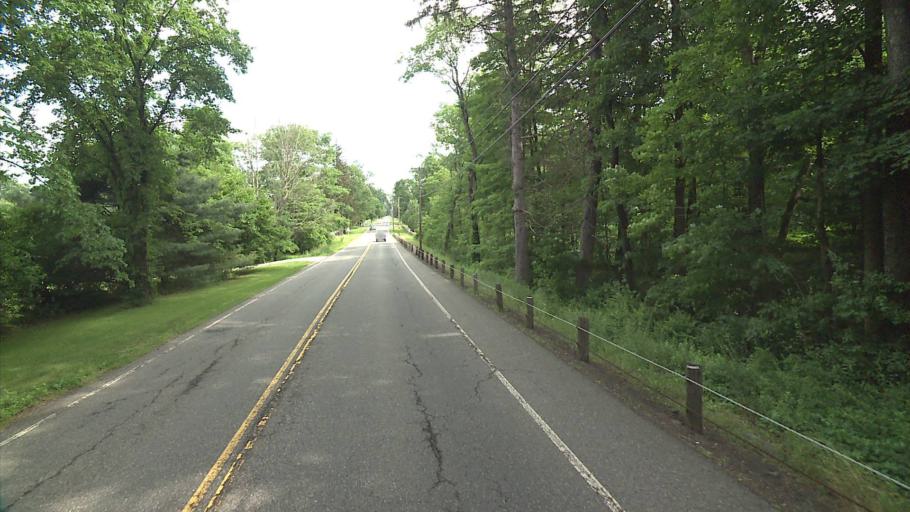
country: US
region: Connecticut
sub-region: Litchfield County
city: Litchfield
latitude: 41.7196
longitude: -73.1863
